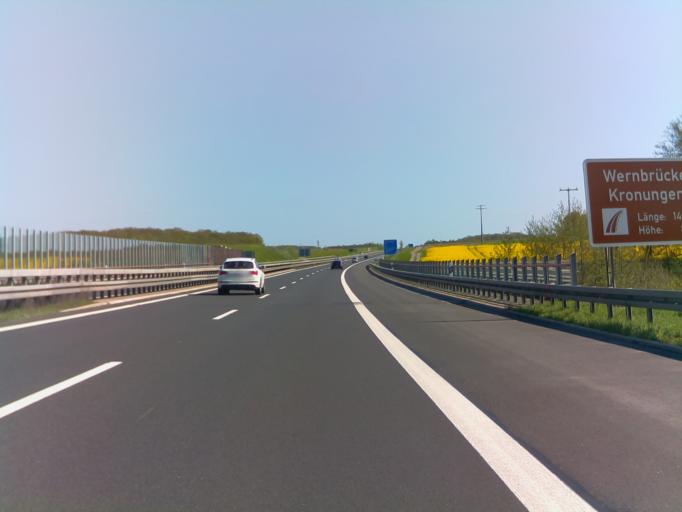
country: DE
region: Bavaria
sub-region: Regierungsbezirk Unterfranken
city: Poppenhausen
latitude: 50.0797
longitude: 10.1493
